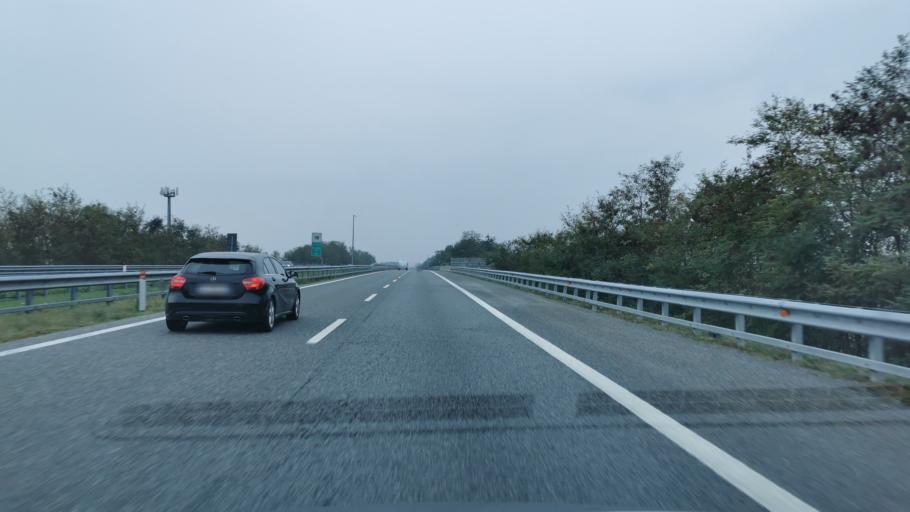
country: IT
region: Piedmont
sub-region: Provincia di Cuneo
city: Caramagna Piemonte
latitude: 44.8091
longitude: 7.7510
